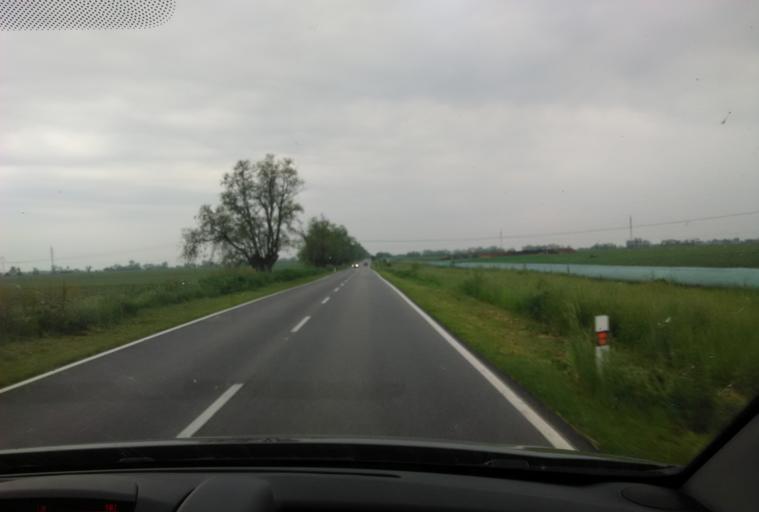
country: SK
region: Trnavsky
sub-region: Okres Trnava
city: Trnava
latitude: 48.4339
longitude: 17.6504
